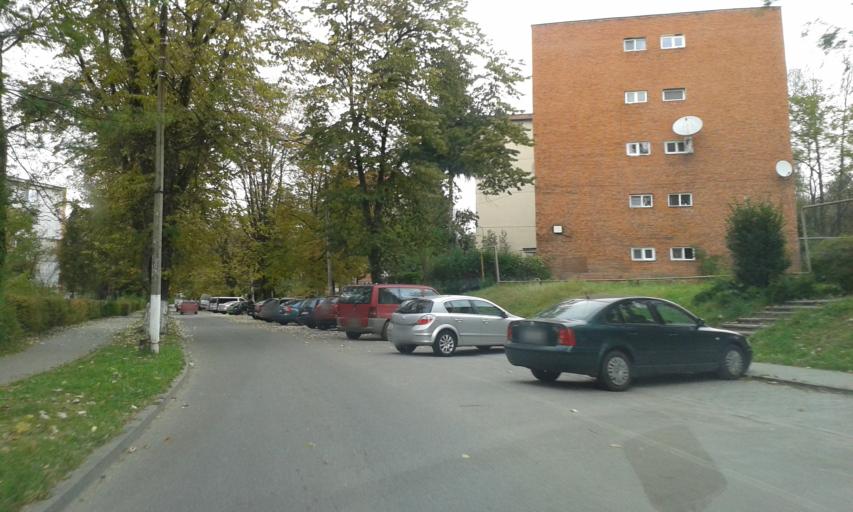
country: RO
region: Hunedoara
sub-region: Municipiul Petrosani
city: Petrosani
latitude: 45.4027
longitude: 23.3772
